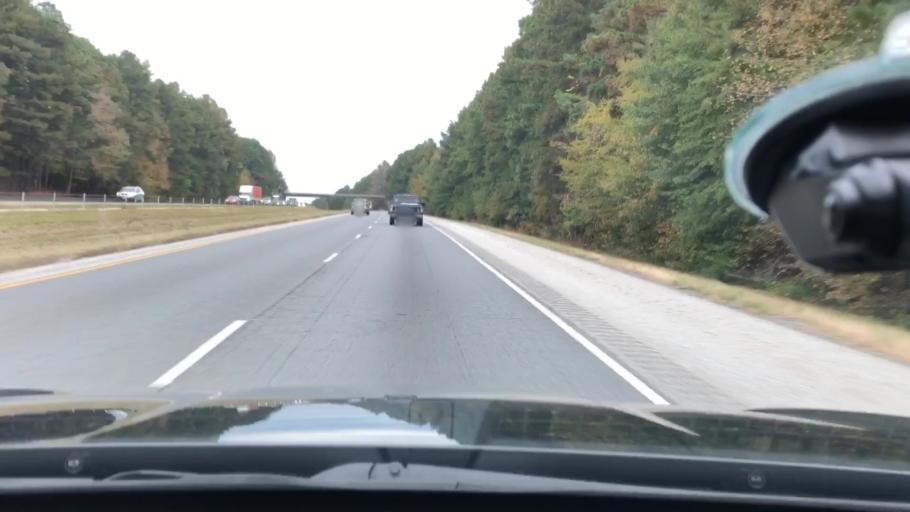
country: US
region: Arkansas
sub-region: Clark County
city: Arkadelphia
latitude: 34.1392
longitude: -93.0817
